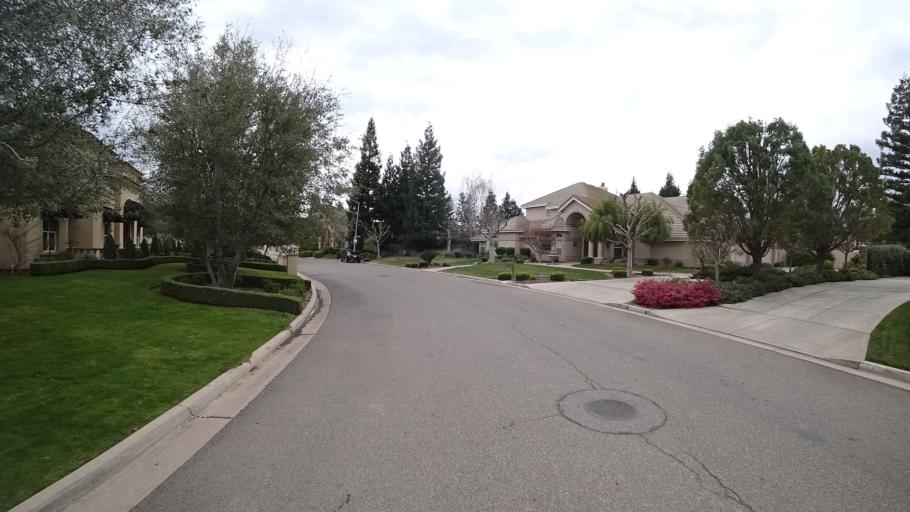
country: US
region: California
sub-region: Fresno County
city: Fresno
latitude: 36.8395
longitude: -119.8337
